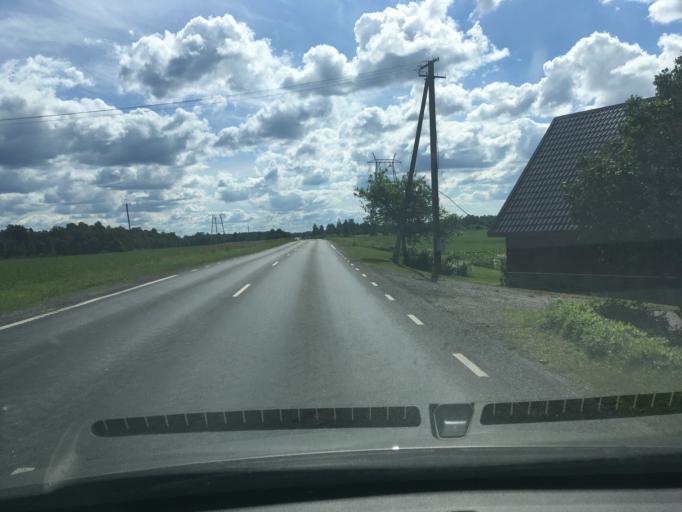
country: EE
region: Laeaene
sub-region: Lihula vald
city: Lihula
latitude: 58.5234
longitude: 24.0722
